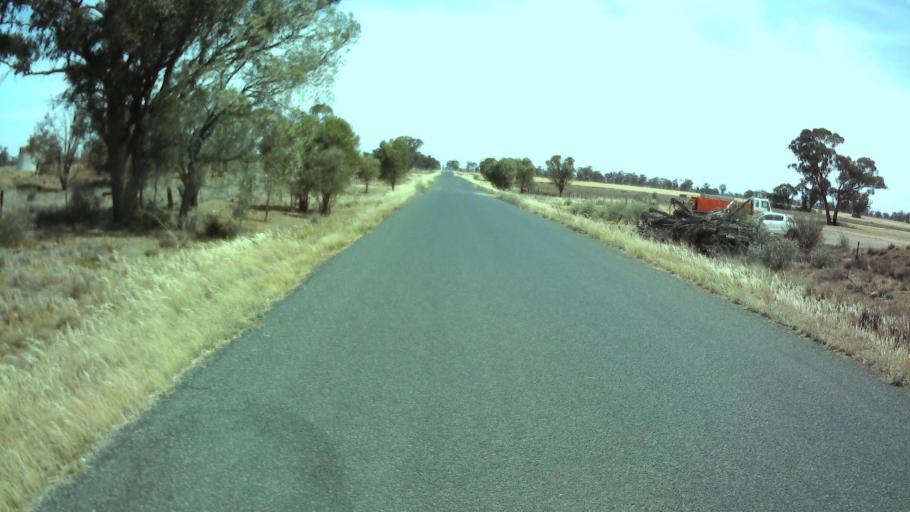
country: AU
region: New South Wales
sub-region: Weddin
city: Grenfell
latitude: -33.9937
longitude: 147.7755
